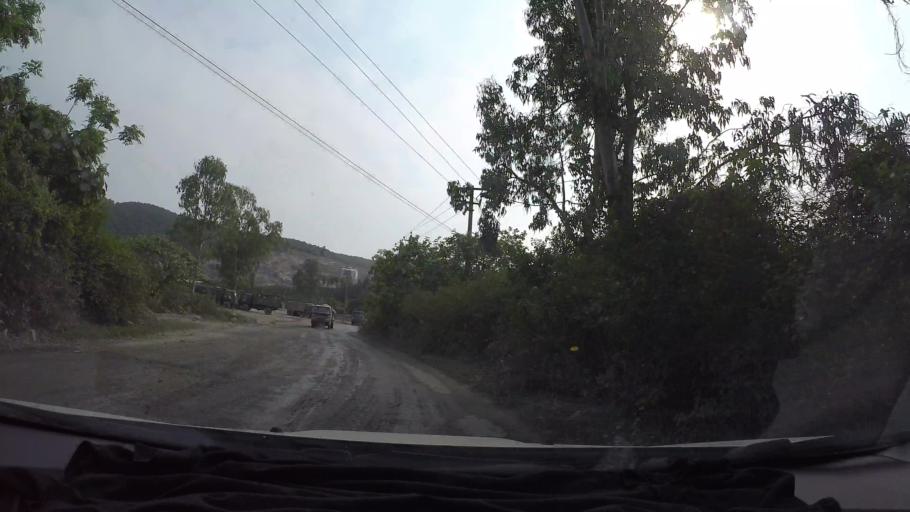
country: VN
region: Da Nang
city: Lien Chieu
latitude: 16.0434
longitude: 108.1499
